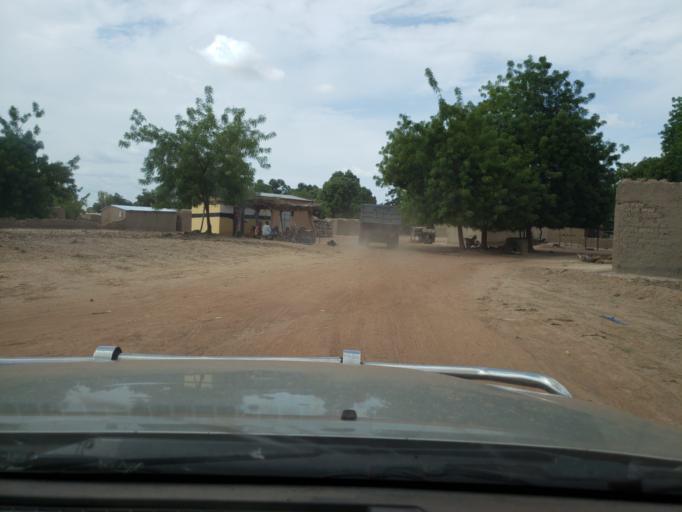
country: ML
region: Segou
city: Bla
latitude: 12.7335
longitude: -5.6688
